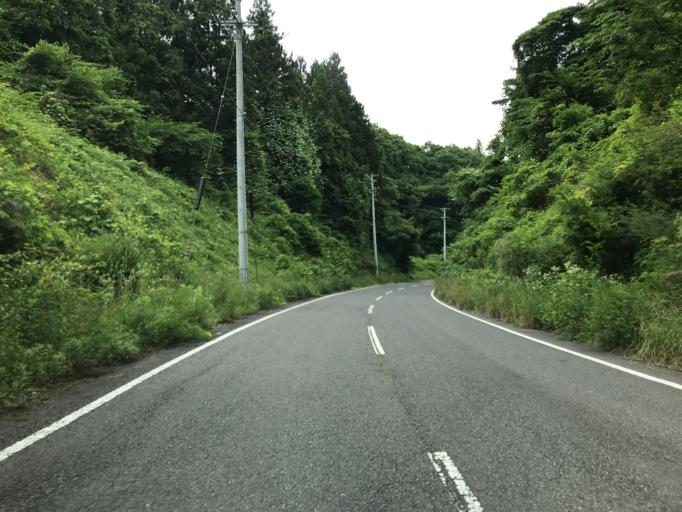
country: JP
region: Fukushima
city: Funehikimachi-funehiki
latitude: 37.4115
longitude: 140.6480
